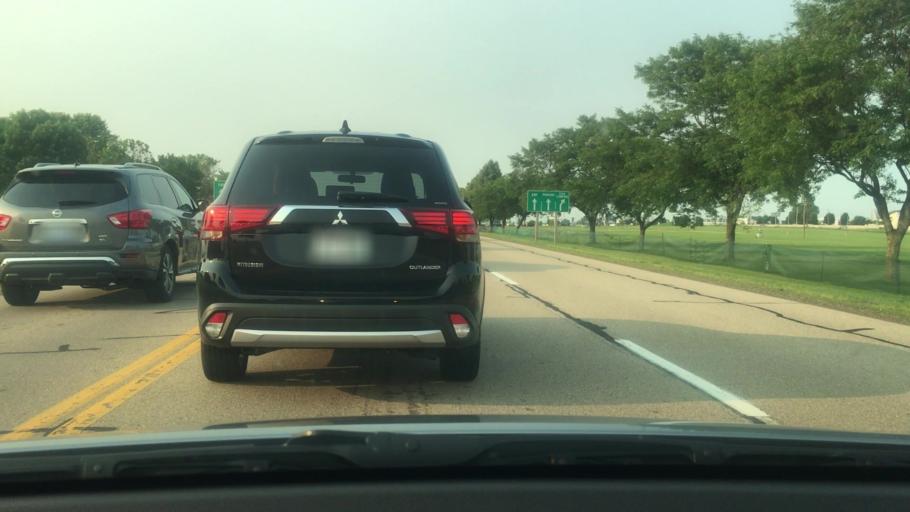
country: US
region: Wisconsin
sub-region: Winnebago County
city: Oshkosh
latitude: 43.9866
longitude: -88.5802
